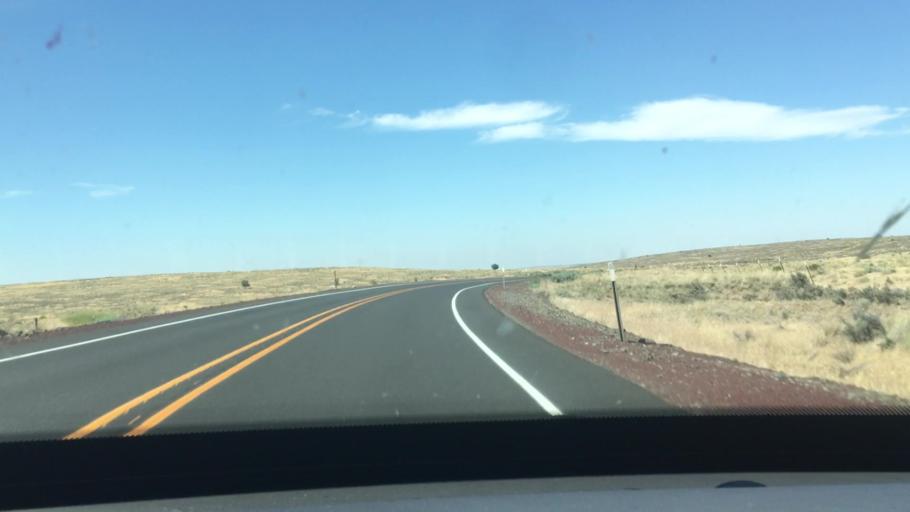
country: US
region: Oregon
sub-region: Sherman County
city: Moro
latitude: 45.0732
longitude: -120.6832
